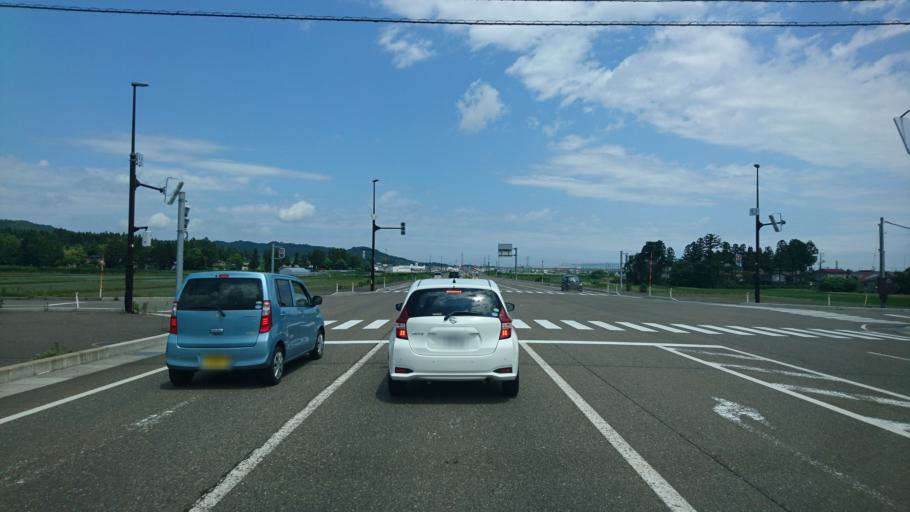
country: JP
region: Niigata
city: Joetsu
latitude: 37.0812
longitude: 138.2343
